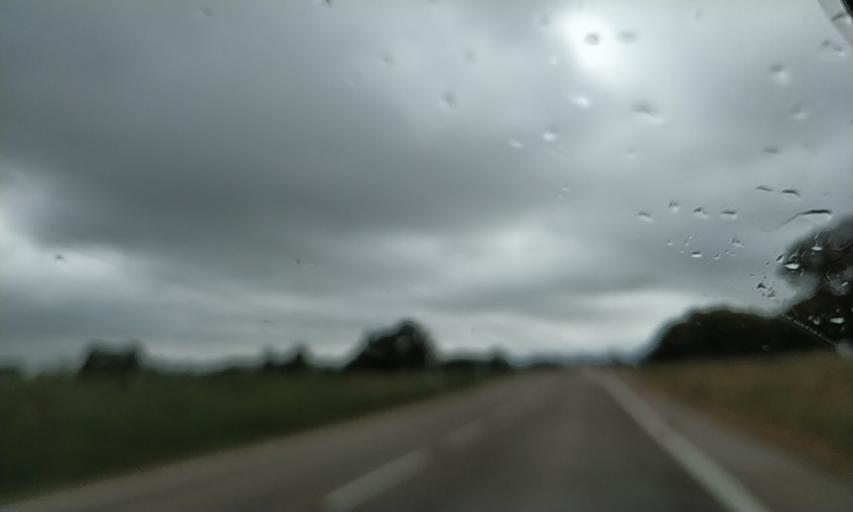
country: ES
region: Extremadura
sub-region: Provincia de Badajoz
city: Villar del Rey
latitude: 39.0428
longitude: -6.8085
